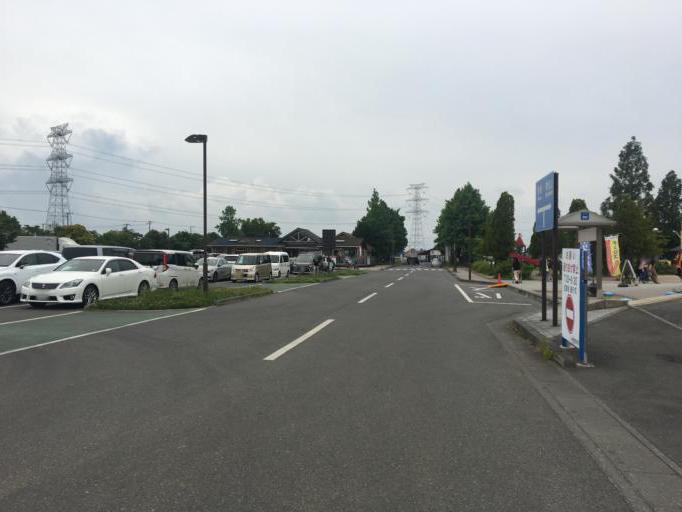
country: JP
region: Saitama
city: Fukiage-fujimi
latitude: 36.0372
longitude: 139.4582
